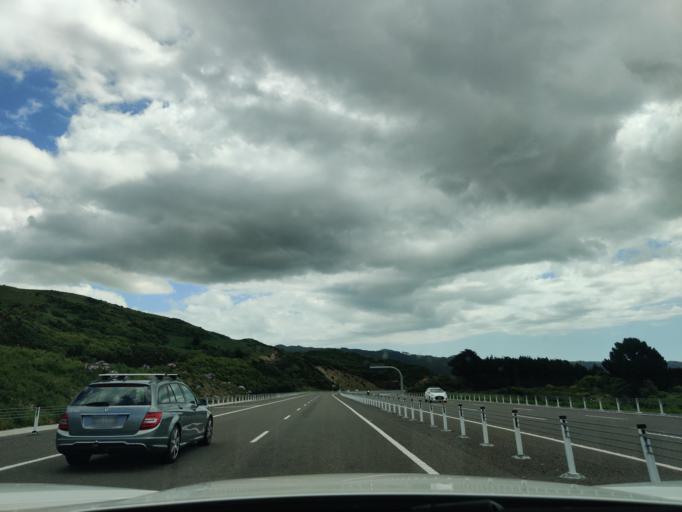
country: NZ
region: Wellington
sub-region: Porirua City
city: Porirua
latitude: -41.1546
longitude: 174.8647
